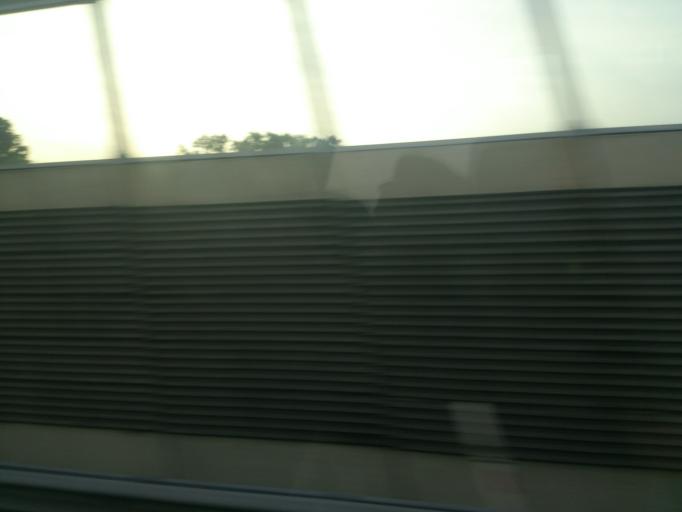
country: IT
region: Lombardy
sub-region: Provincia di Bergamo
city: Azzano San Paolo
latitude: 45.6696
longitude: 9.6663
